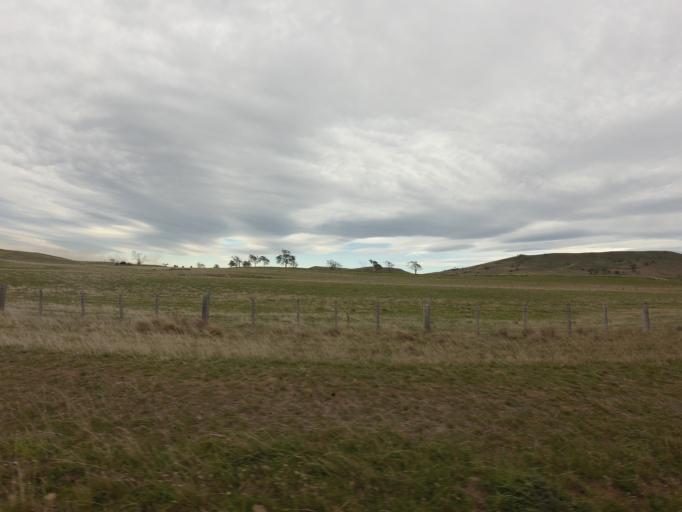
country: AU
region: Tasmania
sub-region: Derwent Valley
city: New Norfolk
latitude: -42.3842
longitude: 146.8719
